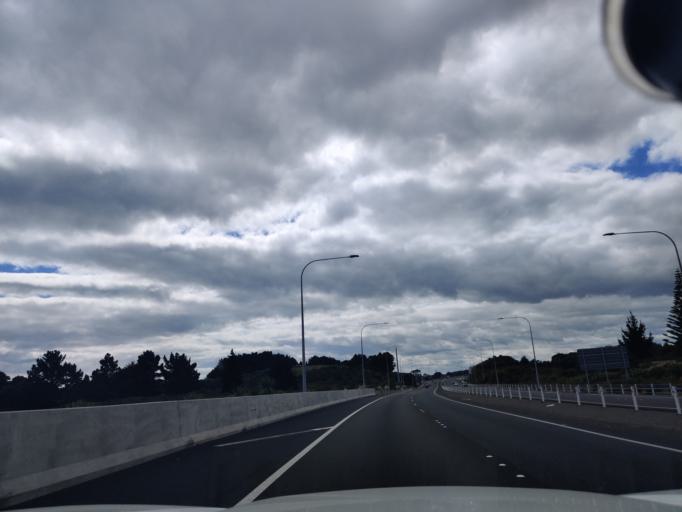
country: NZ
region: Wellington
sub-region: Kapiti Coast District
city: Paraparaumu
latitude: -40.8752
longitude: 175.0283
